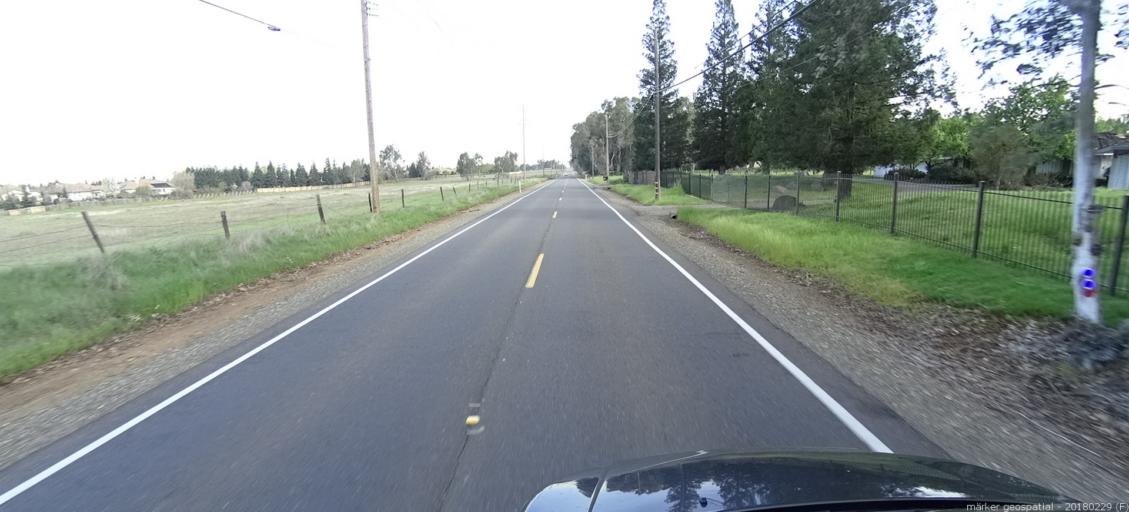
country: US
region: California
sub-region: Sacramento County
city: Vineyard
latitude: 38.4571
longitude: -121.2975
